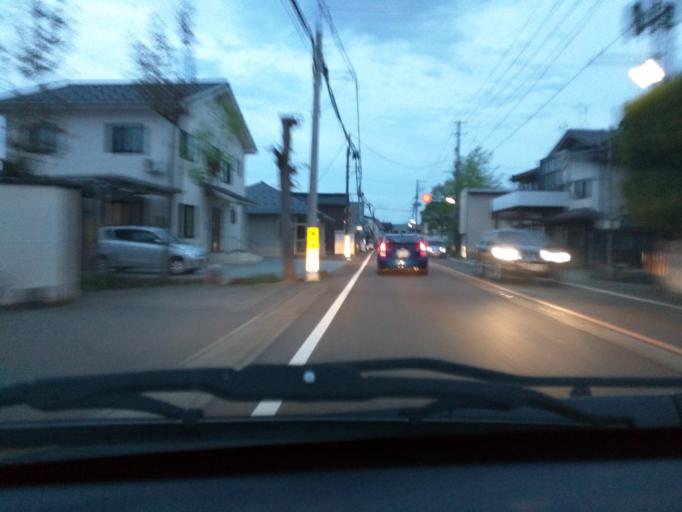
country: JP
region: Niigata
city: Kashiwazaki
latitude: 37.3388
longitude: 138.6156
